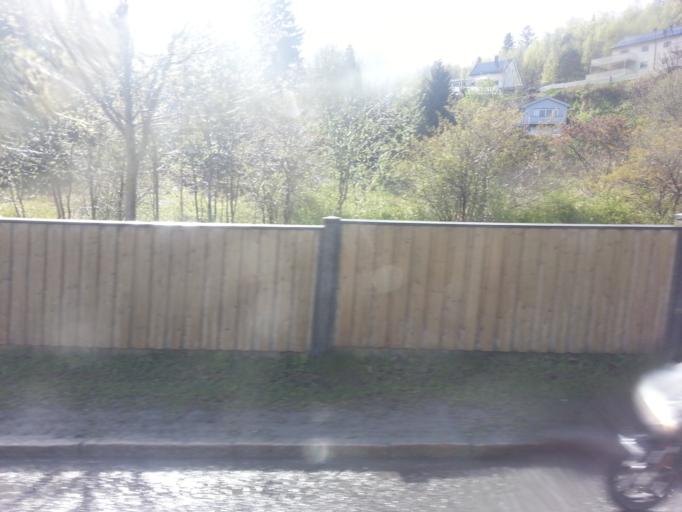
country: NO
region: Sor-Trondelag
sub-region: Trondheim
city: Trondheim
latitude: 63.3995
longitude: 10.3583
